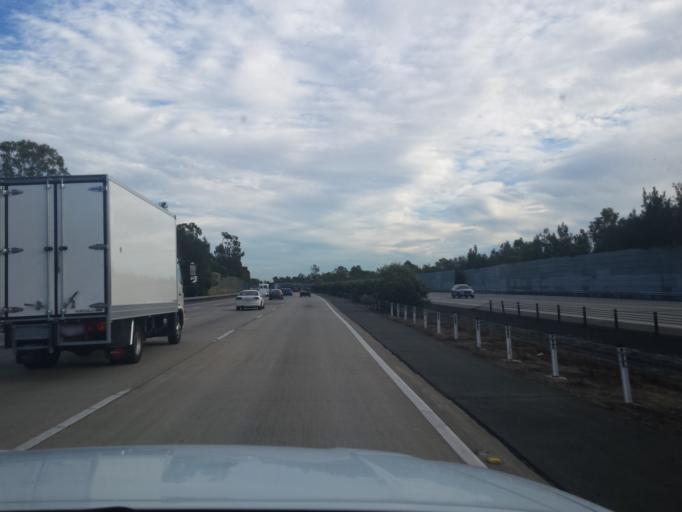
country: AU
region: Queensland
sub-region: Gold Coast
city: Ormeau Hills
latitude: -27.7947
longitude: 153.2602
